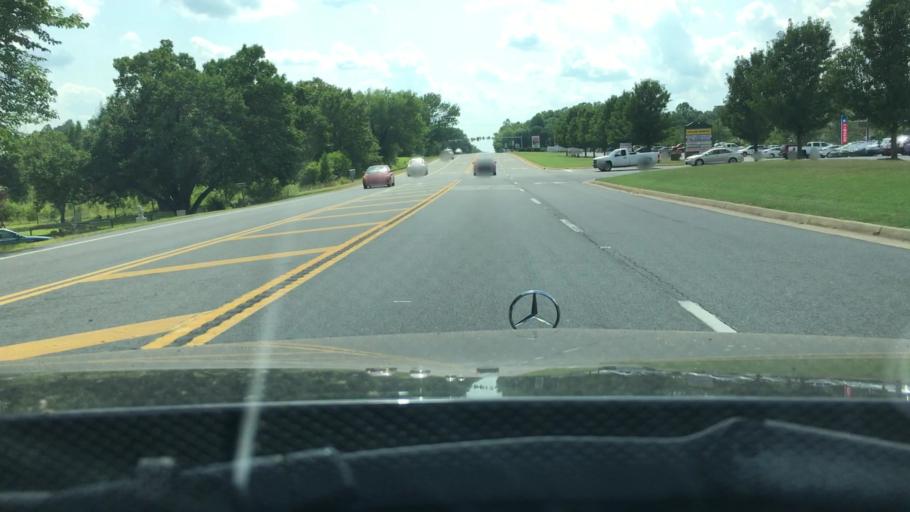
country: US
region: Virginia
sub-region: Spotsylvania County
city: Spotsylvania
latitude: 38.3058
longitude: -77.8065
